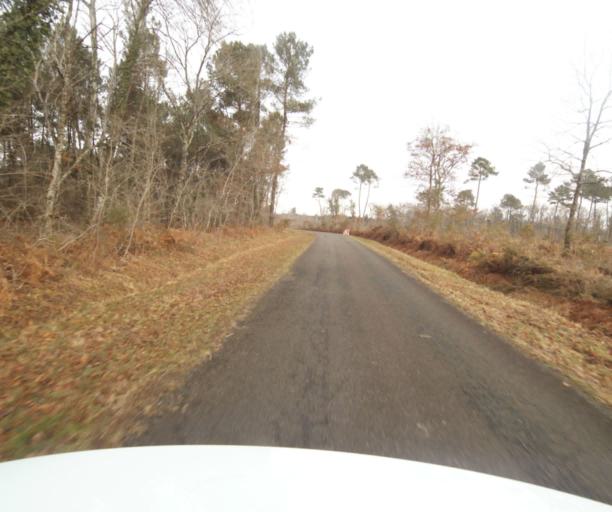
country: FR
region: Aquitaine
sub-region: Departement des Landes
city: Gabarret
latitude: 44.0851
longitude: 0.0715
